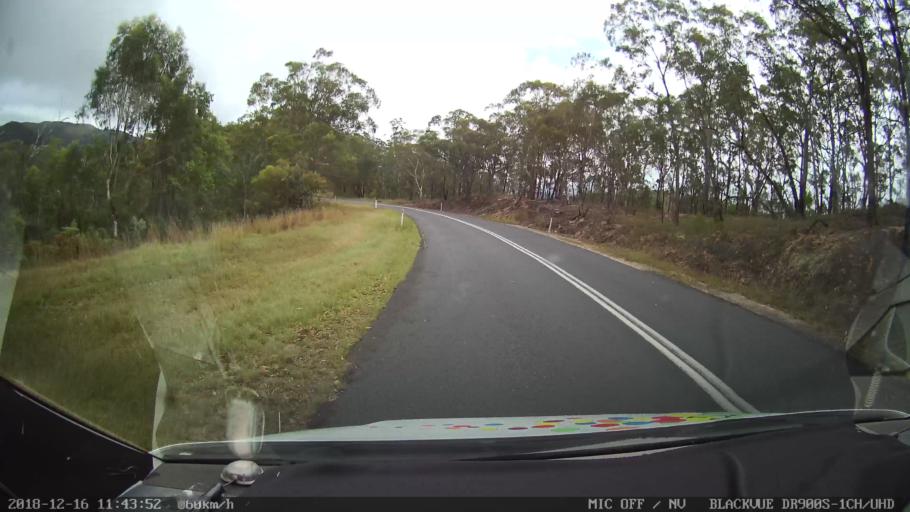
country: AU
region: New South Wales
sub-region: Tenterfield Municipality
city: Carrolls Creek
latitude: -28.9431
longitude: 152.2201
